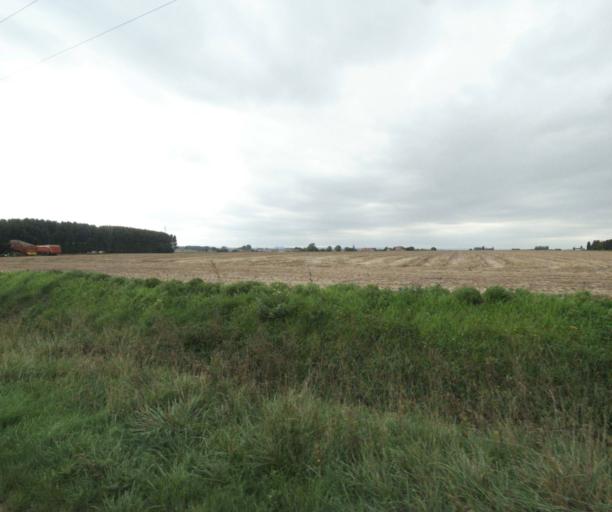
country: FR
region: Nord-Pas-de-Calais
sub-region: Departement du Nord
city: Herlies
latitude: 50.5672
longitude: 2.8575
